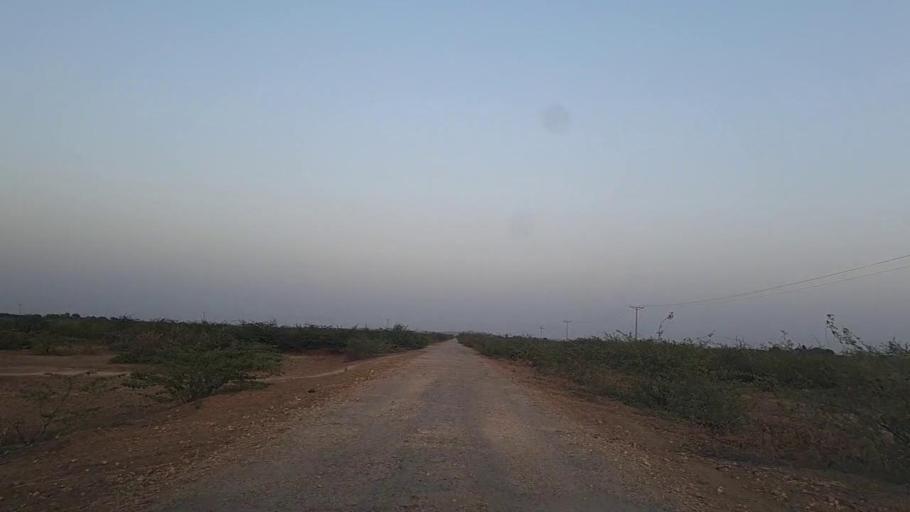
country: PK
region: Sindh
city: Naukot
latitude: 24.7200
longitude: 69.2924
